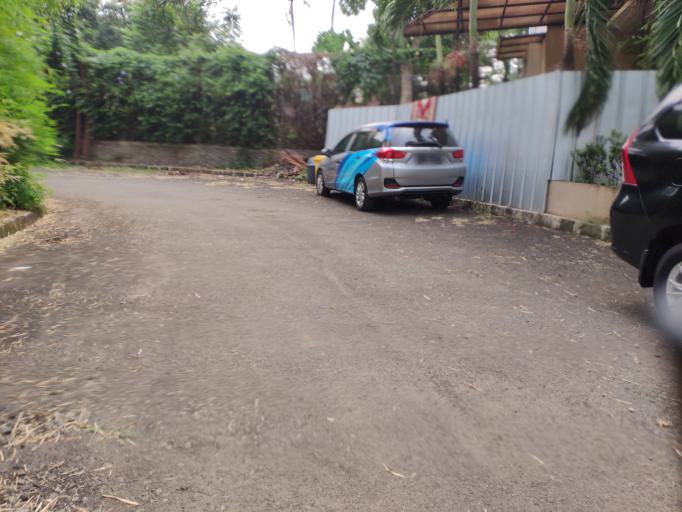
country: ID
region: West Java
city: Pamulang
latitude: -6.3243
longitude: 106.8050
